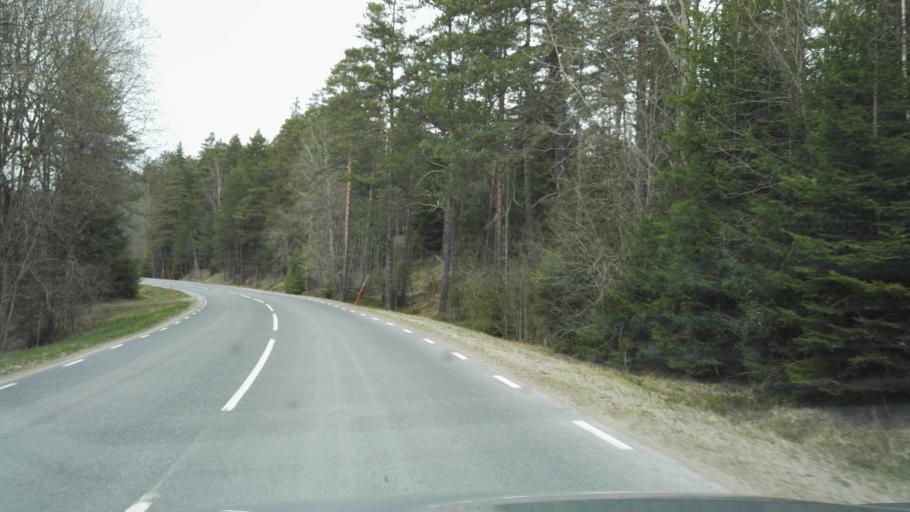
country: SE
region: Joenkoeping
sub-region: Vetlanda Kommun
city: Landsbro
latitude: 57.2623
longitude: 14.9350
